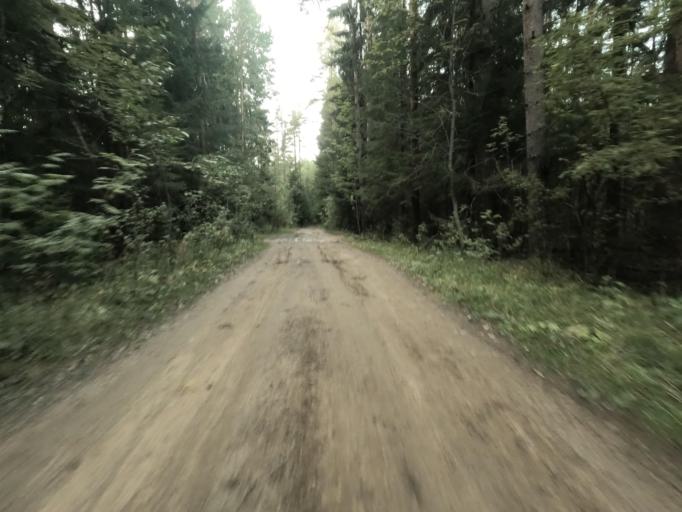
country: RU
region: Leningrad
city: Otradnoye
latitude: 59.8472
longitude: 30.7972
